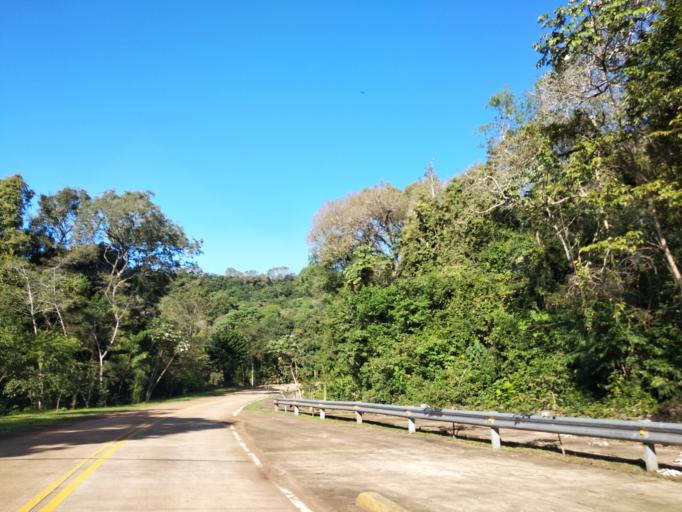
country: AR
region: Misiones
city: Cerro Cora
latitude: -27.4556
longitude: -55.5647
